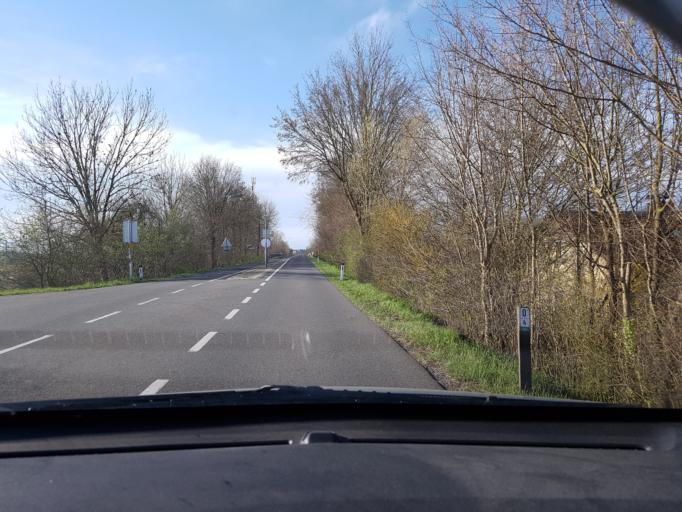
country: AT
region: Upper Austria
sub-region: Politischer Bezirk Linz-Land
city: Asten
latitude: 48.2152
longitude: 14.4197
